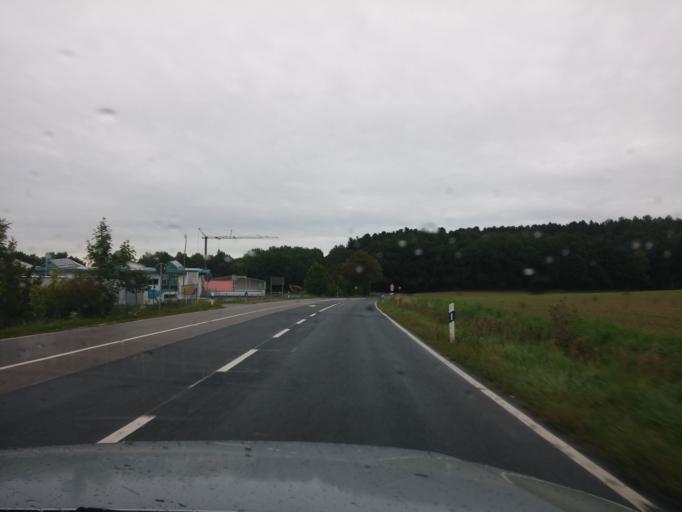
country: DE
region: Bavaria
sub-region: Upper Bavaria
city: Hohenkammer
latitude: 48.4268
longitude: 11.5594
